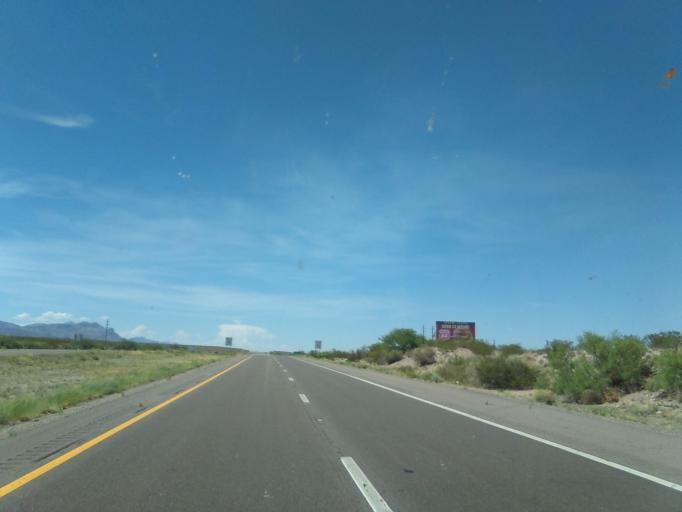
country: US
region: New Mexico
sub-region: Socorro County
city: Socorro
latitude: 33.9237
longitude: -106.8791
